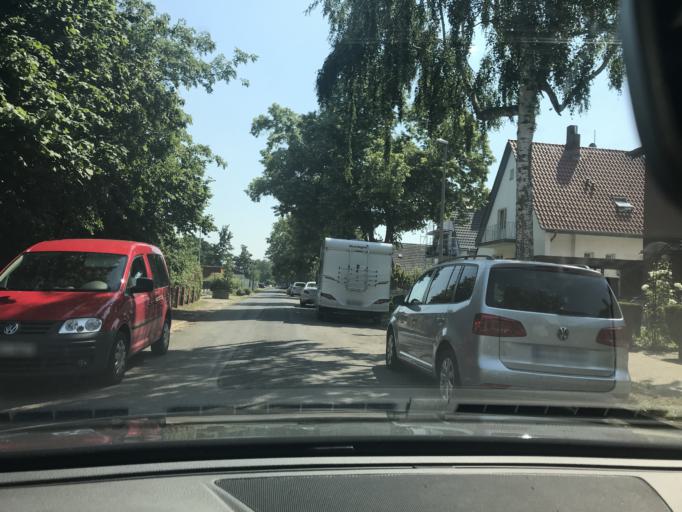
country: DE
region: Lower Saxony
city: Sehnde
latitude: 52.3466
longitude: 9.9435
